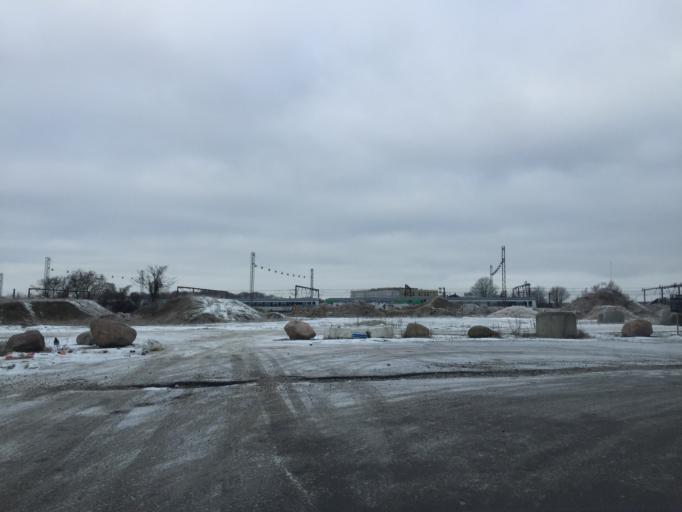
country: DK
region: South Denmark
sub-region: Odense Kommune
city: Odense
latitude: 55.4001
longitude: 10.3798
